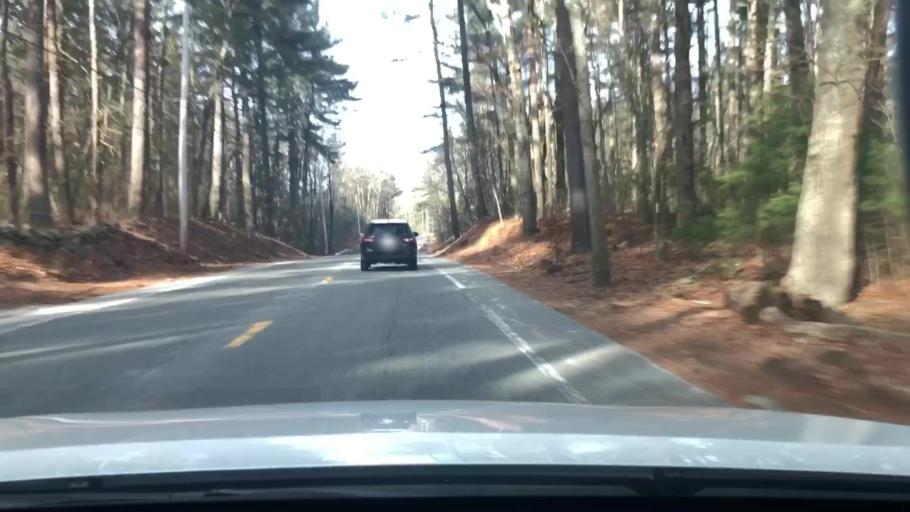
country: US
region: Massachusetts
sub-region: Worcester County
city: Grafton
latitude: 42.1965
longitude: -71.6564
